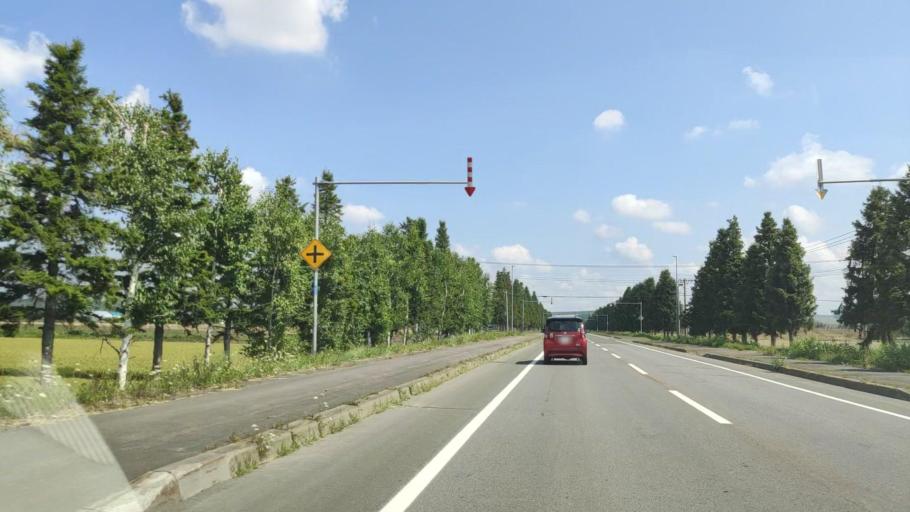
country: JP
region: Hokkaido
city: Shimo-furano
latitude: 43.4793
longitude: 142.4592
